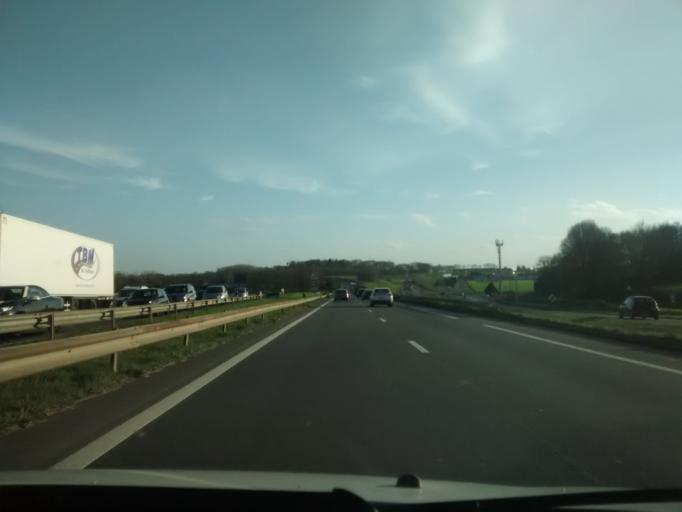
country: FR
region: Brittany
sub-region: Departement d'Ille-et-Vilaine
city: Saint-Jacques-de-la-Lande
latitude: 48.0834
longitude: -1.6983
